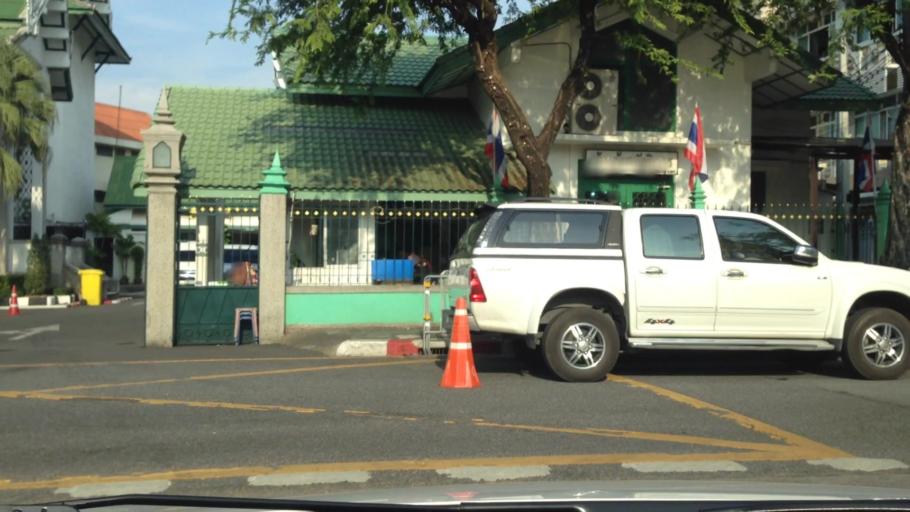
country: TH
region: Bangkok
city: Pom Prap Sattru Phai
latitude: 13.7583
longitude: 100.5067
